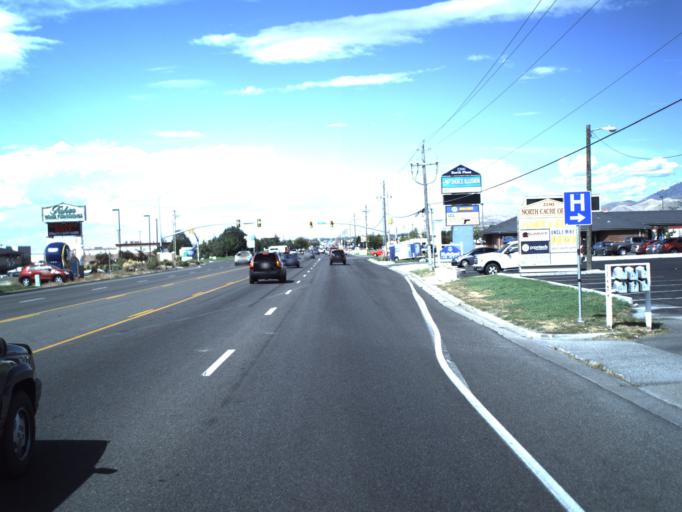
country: US
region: Utah
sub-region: Cache County
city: North Logan
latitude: 41.7709
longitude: -111.8340
